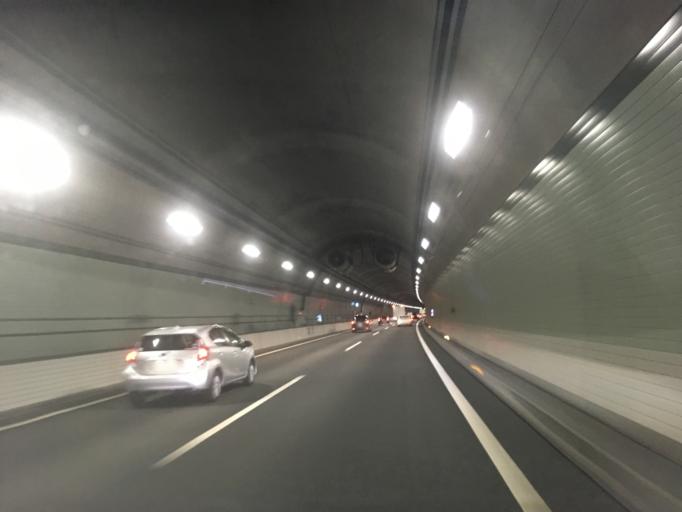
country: JP
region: Tokyo
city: Hachioji
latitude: 35.6464
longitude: 139.2514
